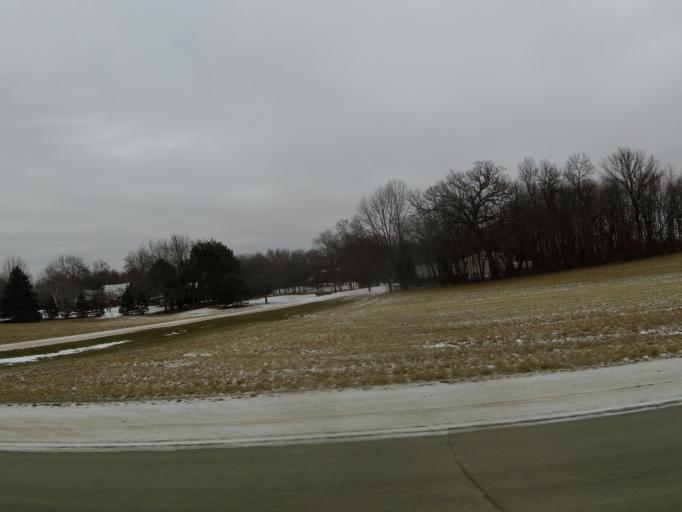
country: US
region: Minnesota
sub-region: Wright County
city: Montrose
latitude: 45.0584
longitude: -93.8591
